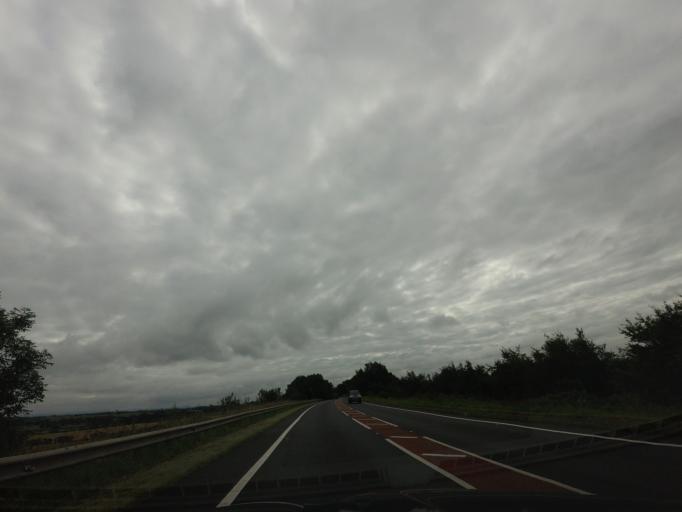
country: GB
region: Scotland
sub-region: Dumfries and Galloway
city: Gretna
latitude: 54.9930
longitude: -3.1184
